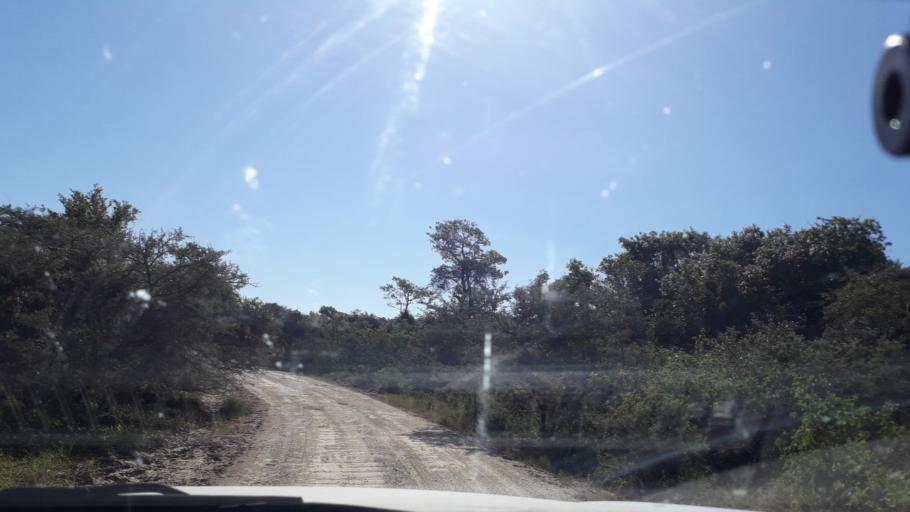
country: ZA
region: Eastern Cape
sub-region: Amathole District Municipality
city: Komga
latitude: -32.7680
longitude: 27.9628
